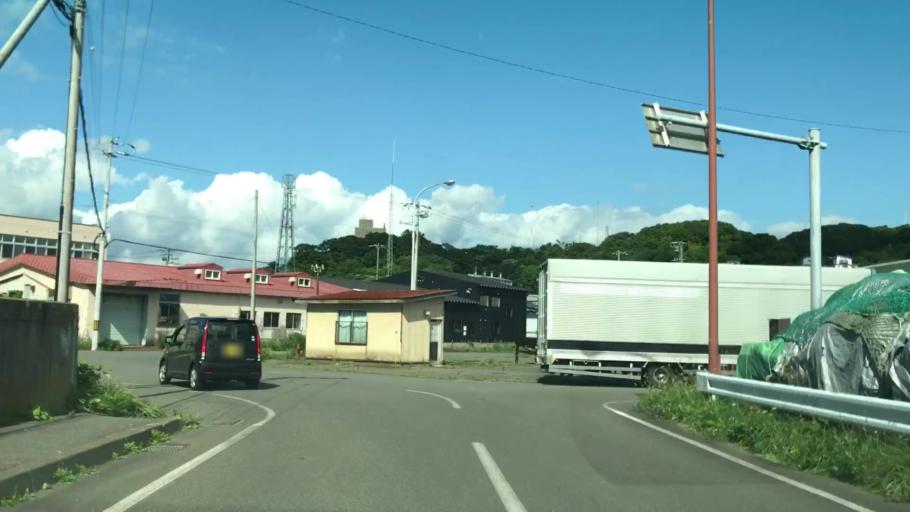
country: JP
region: Hokkaido
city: Muroran
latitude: 42.3086
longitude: 140.9710
